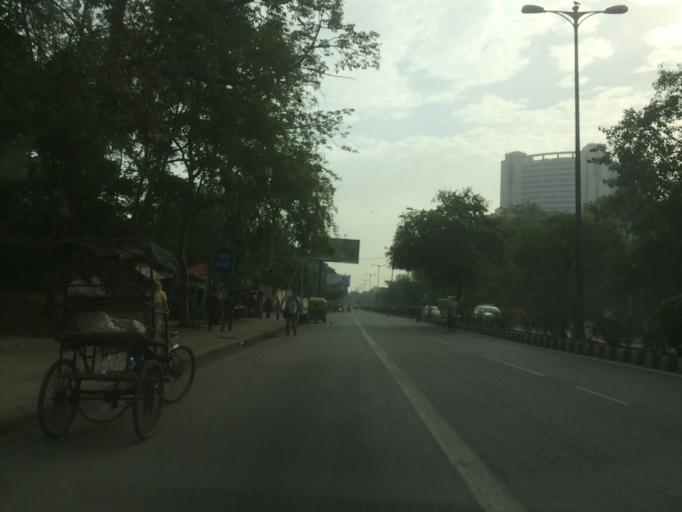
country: IN
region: NCT
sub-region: New Delhi
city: New Delhi
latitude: 28.6387
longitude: 77.2240
